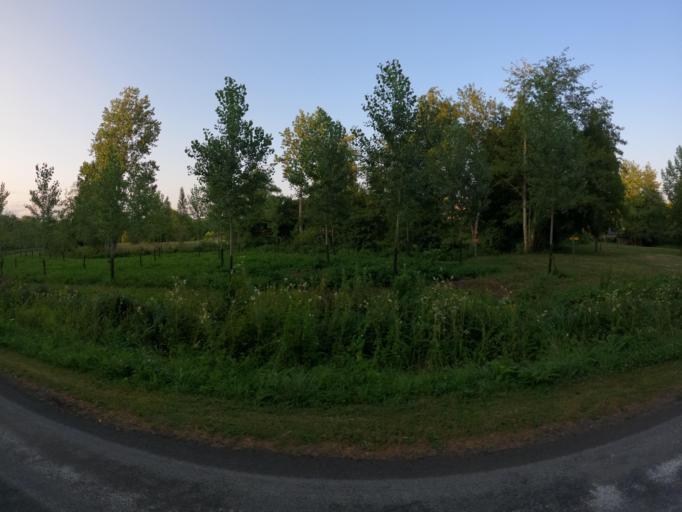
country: FR
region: Pays de la Loire
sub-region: Departement de la Sarthe
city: Parce-sur-Sarthe
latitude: 47.8679
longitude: -0.2113
